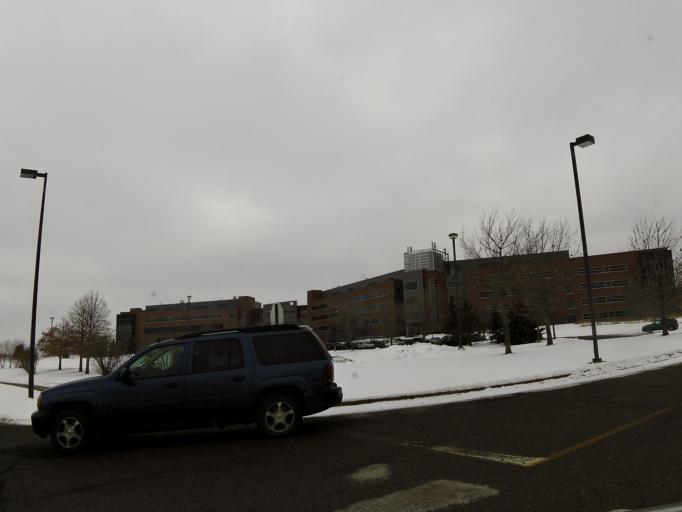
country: US
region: Minnesota
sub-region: Washington County
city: Oakdale
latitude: 45.0024
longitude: -92.9499
